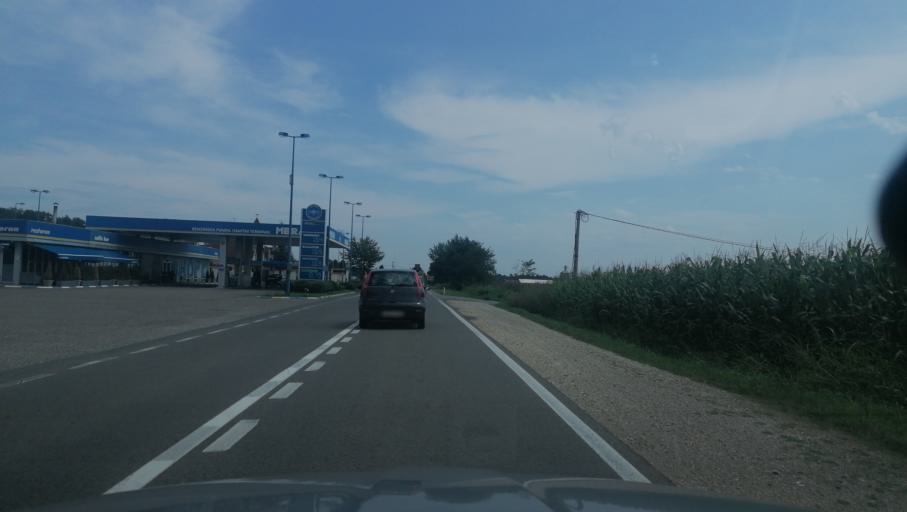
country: HR
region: Vukovarsko-Srijemska
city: Soljani
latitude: 44.8334
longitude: 18.9860
